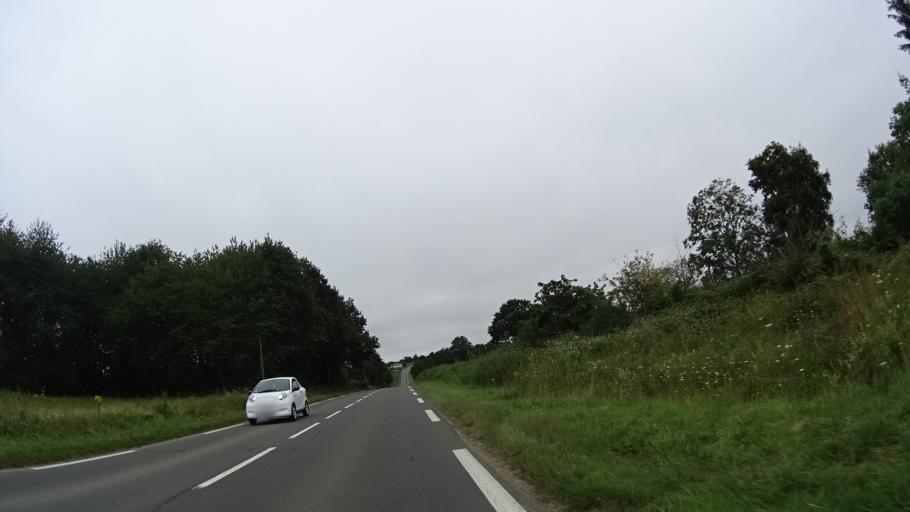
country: FR
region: Brittany
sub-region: Departement d'Ille-et-Vilaine
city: Vignoc
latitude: 48.2535
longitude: -1.8295
